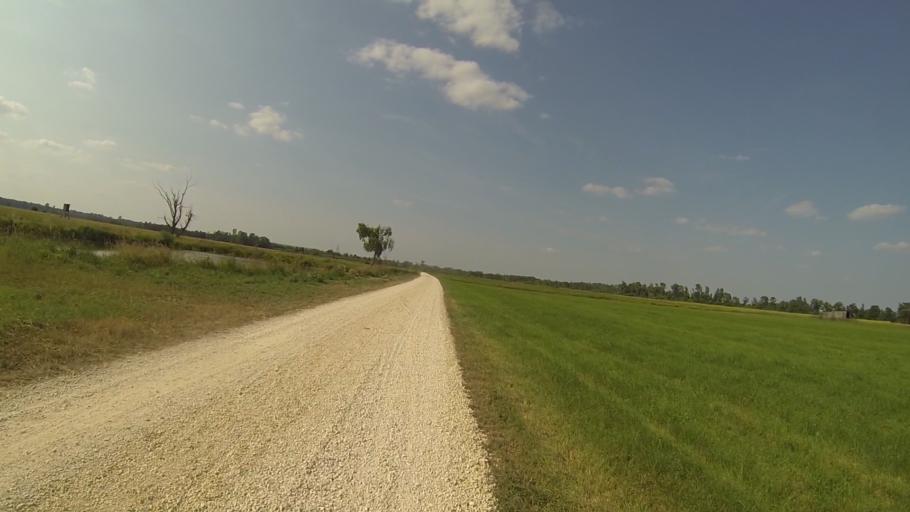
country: DE
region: Bavaria
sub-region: Swabia
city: Leipheim
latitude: 48.4711
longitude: 10.1988
